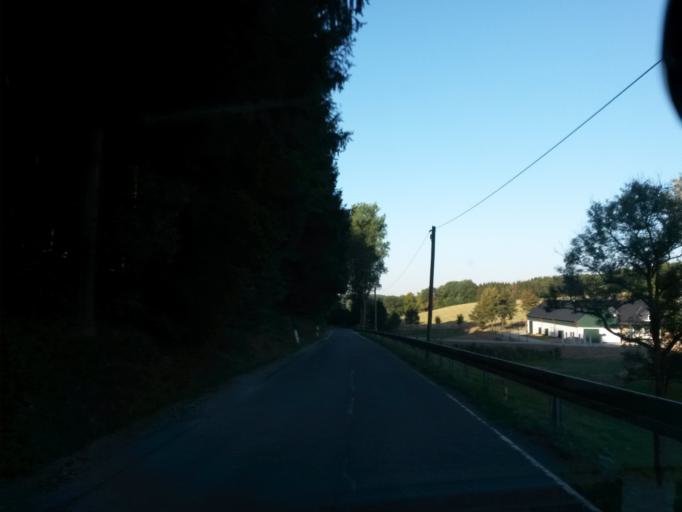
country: DE
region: North Rhine-Westphalia
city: Wipperfurth
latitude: 51.0828
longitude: 7.3970
